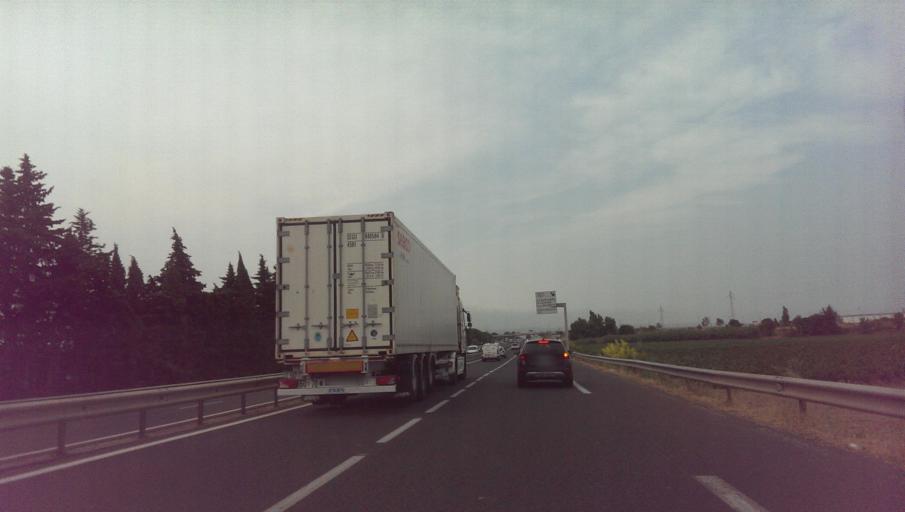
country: FR
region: Languedoc-Roussillon
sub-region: Departement des Pyrenees-Orientales
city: Rivesaltes
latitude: 42.7742
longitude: 2.9019
